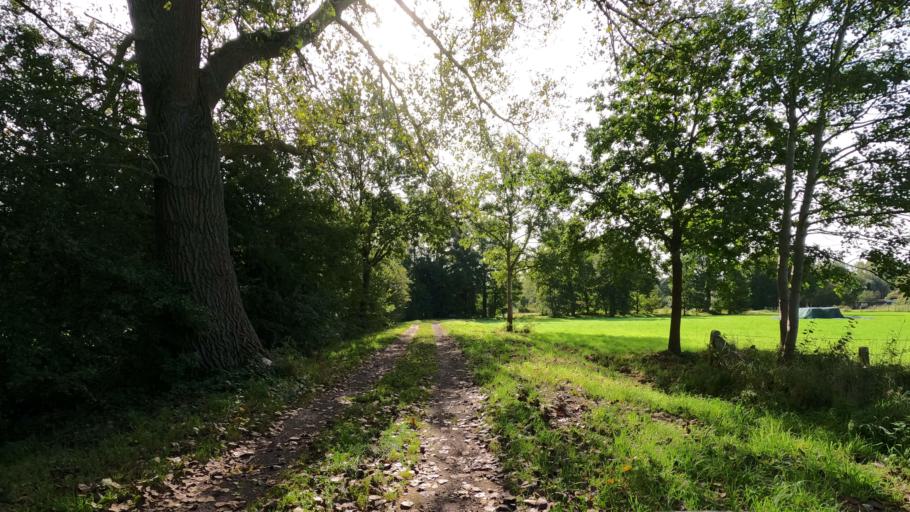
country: BE
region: Flanders
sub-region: Provincie Antwerpen
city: Hulshout
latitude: 51.0669
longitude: 4.8370
